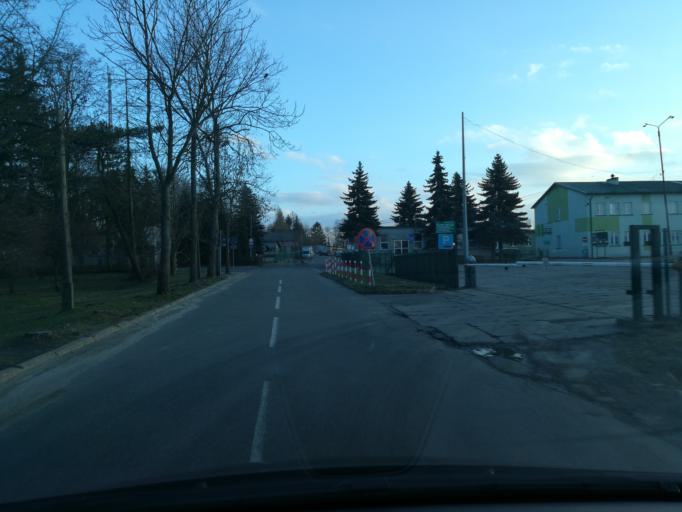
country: PL
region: Lodz Voivodeship
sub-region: Piotrkow Trybunalski
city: Piotrkow Trybunalski
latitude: 51.4053
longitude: 19.6469
